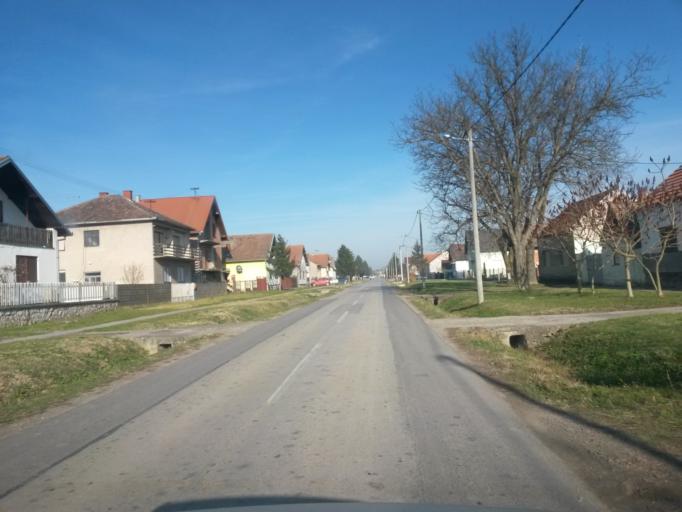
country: HR
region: Vukovarsko-Srijemska
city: Mirkovci
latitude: 45.2420
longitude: 18.8980
